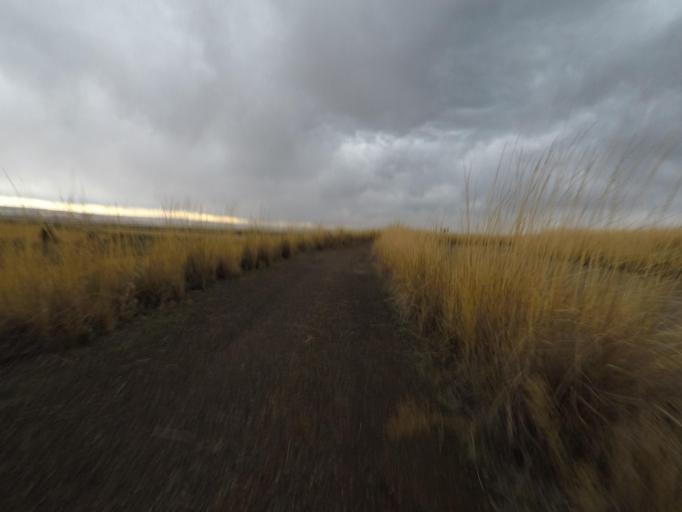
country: US
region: Washington
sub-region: Walla Walla County
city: Walla Walla East
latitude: 46.0629
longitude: -118.2667
